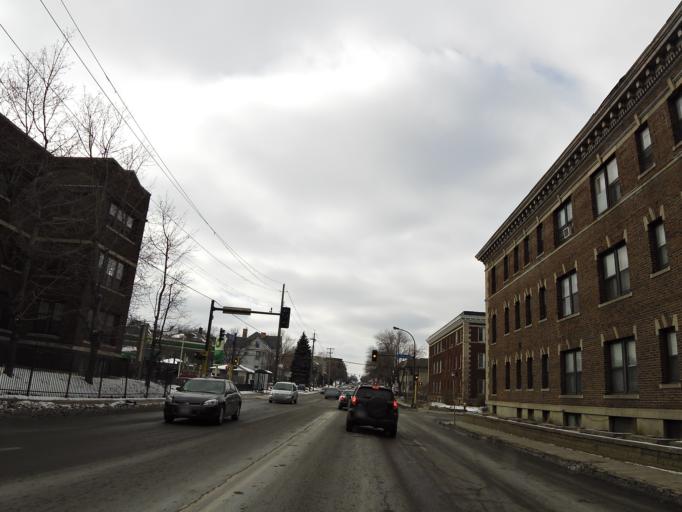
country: US
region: Minnesota
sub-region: Hennepin County
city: Minneapolis
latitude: 44.9627
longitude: -93.2722
